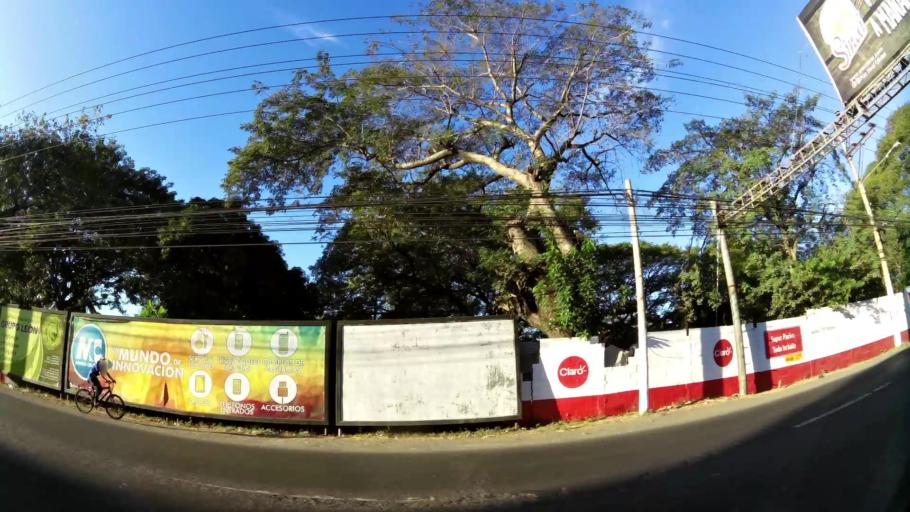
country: SV
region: San Miguel
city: San Miguel
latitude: 13.4706
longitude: -88.1827
